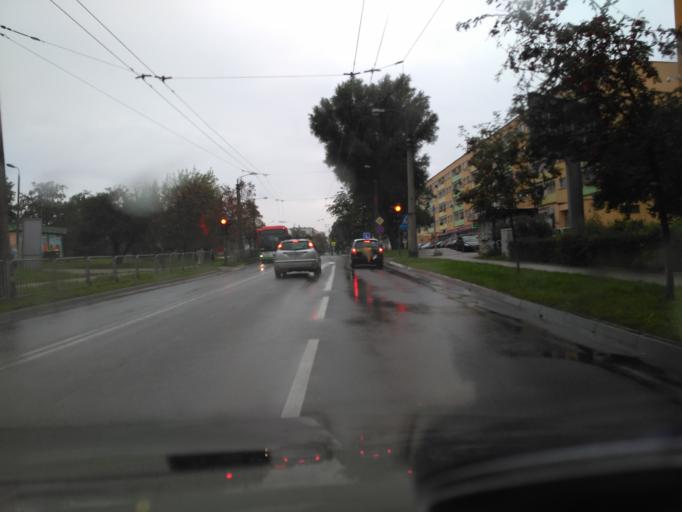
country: PL
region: Lublin Voivodeship
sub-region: Powiat lubelski
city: Lublin
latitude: 51.2438
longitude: 22.5982
